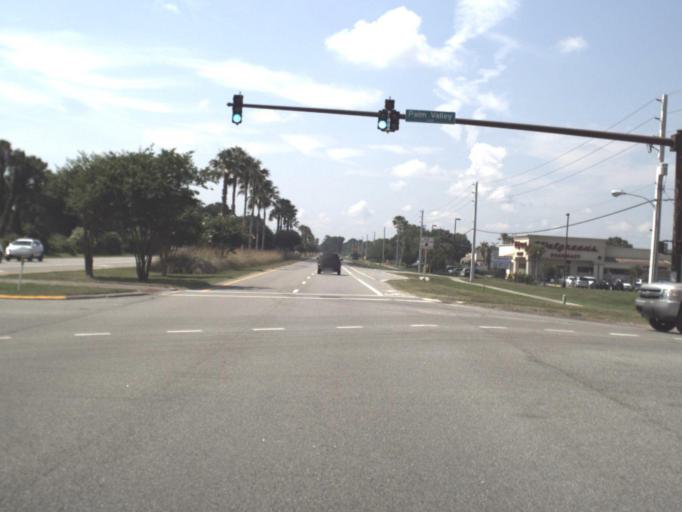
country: US
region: Florida
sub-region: Saint Johns County
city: Sawgrass
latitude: 30.1950
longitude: -81.3808
